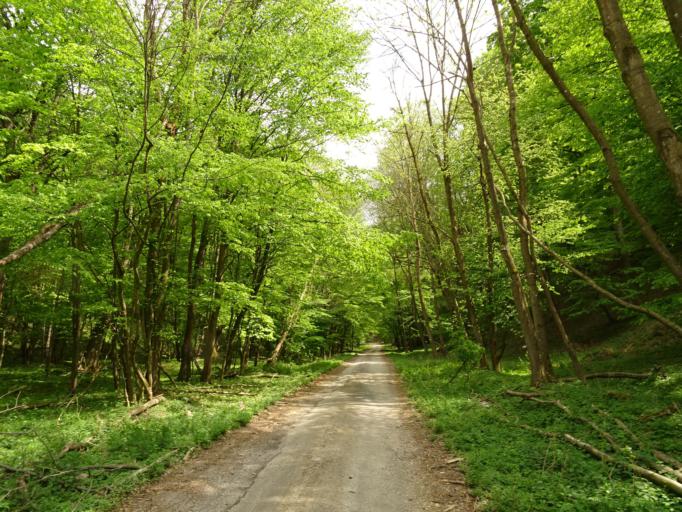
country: HU
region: Fejer
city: Szarliget
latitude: 47.4608
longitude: 18.4532
